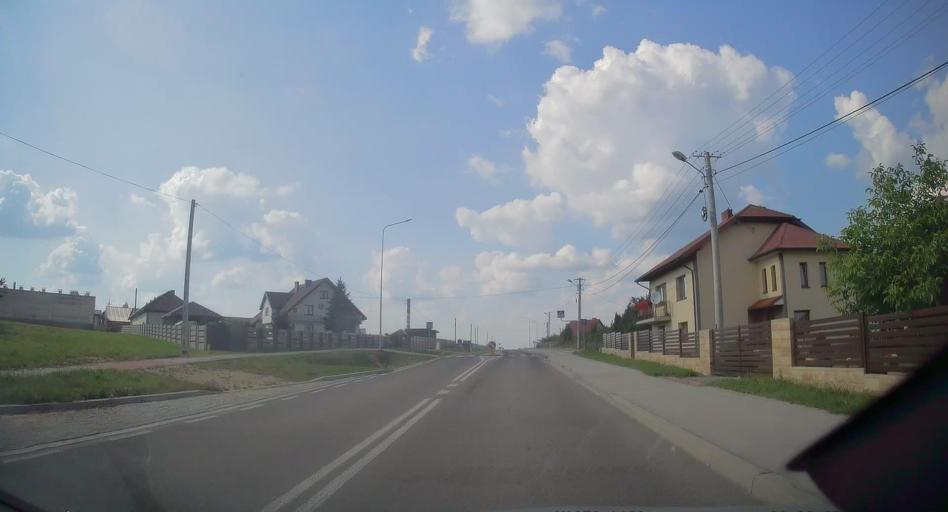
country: PL
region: Swietokrzyskie
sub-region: Powiat konecki
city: Radoszyce
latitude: 51.0330
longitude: 20.2874
